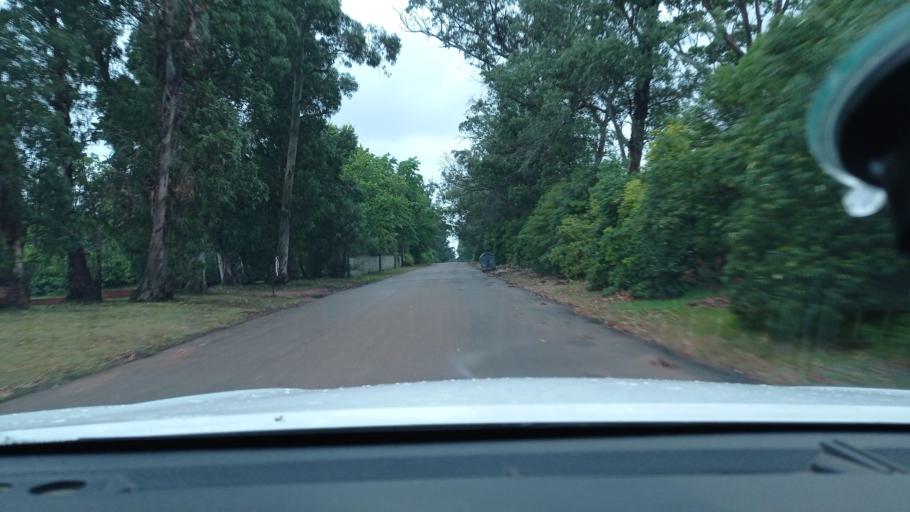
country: UY
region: Maldonado
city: Maldonado
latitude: -34.9170
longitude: -54.9117
